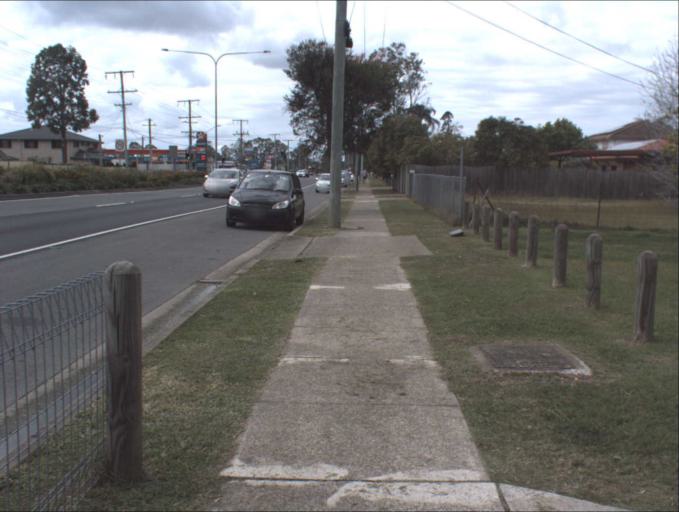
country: AU
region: Queensland
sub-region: Logan
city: Waterford West
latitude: -27.6917
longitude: 153.1325
